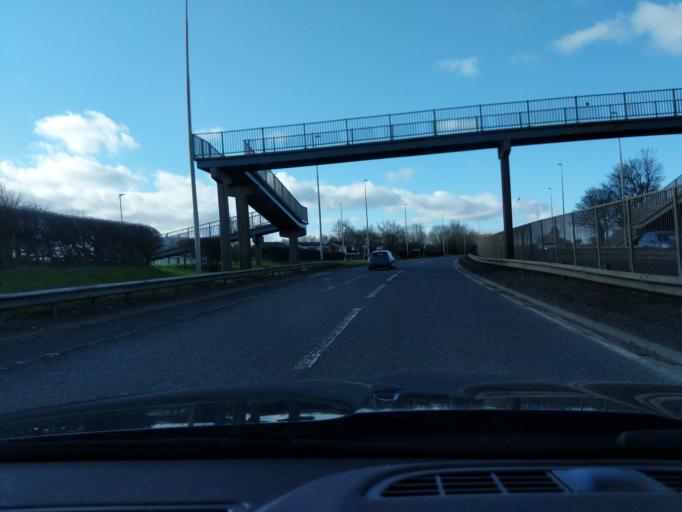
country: GB
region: England
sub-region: South Tyneside
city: Hebburn
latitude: 54.9561
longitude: -1.4951
